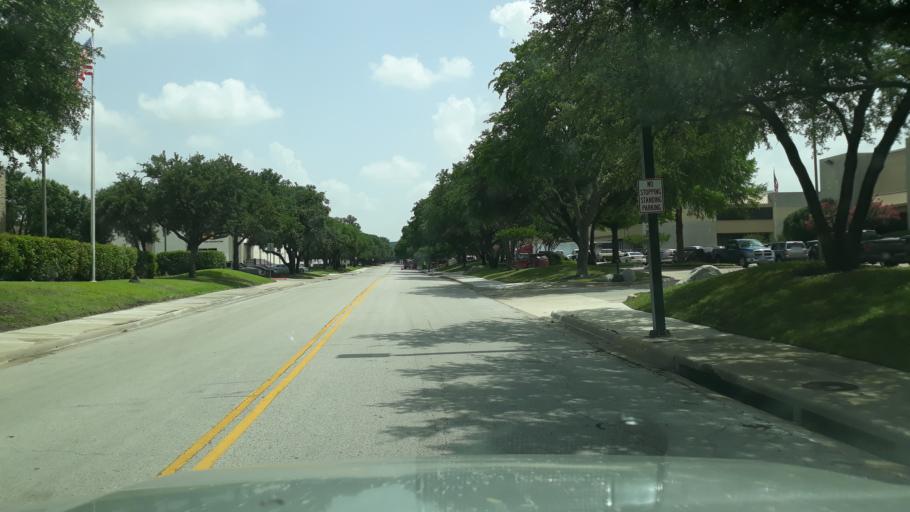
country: US
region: Texas
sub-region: Dallas County
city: Coppell
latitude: 32.9330
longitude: -97.0171
